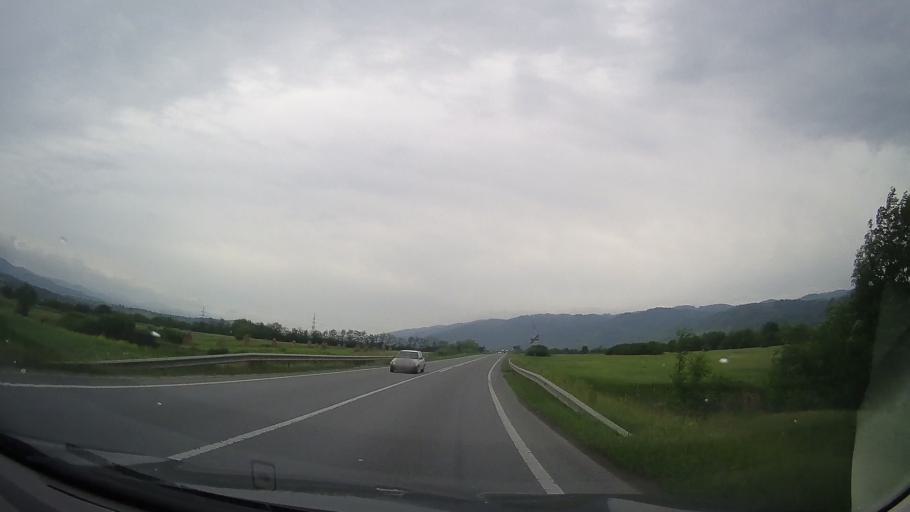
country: RO
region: Caras-Severin
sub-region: Comuna Bucosnita
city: Bucosnita
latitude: 45.2845
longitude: 22.2941
